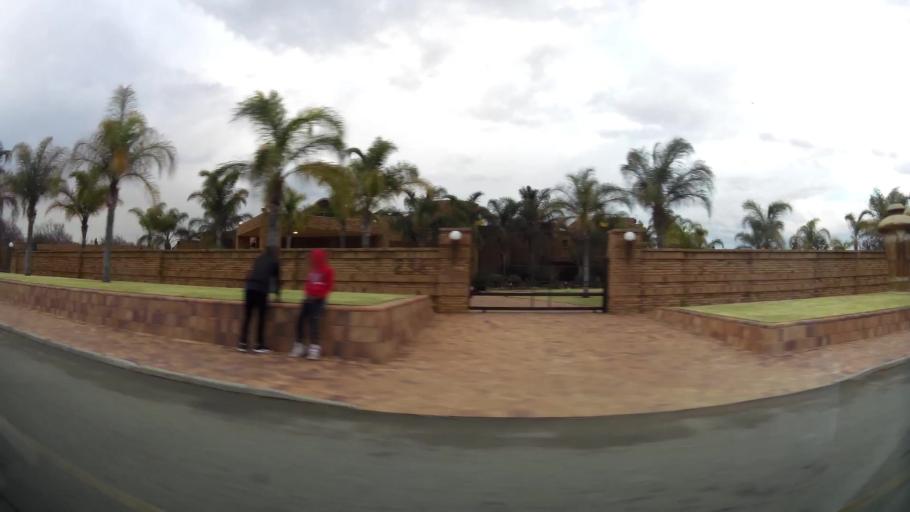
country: ZA
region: Orange Free State
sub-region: Lejweleputswa District Municipality
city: Welkom
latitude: -27.9575
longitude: 26.7365
